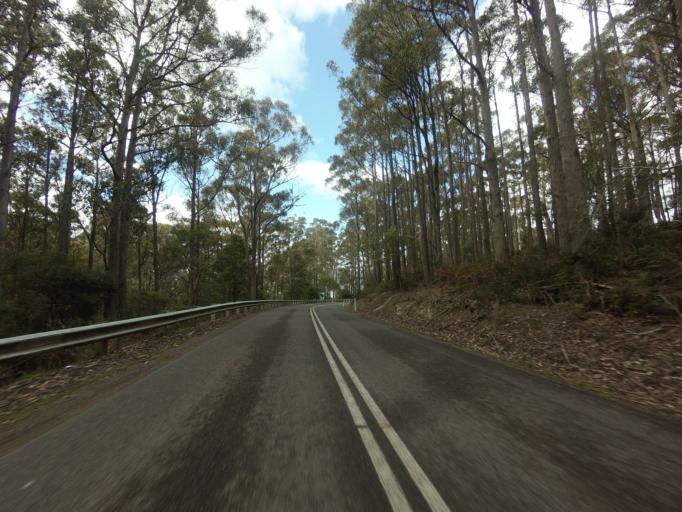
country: AU
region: Tasmania
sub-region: Huon Valley
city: Geeveston
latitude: -43.1969
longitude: 146.9523
